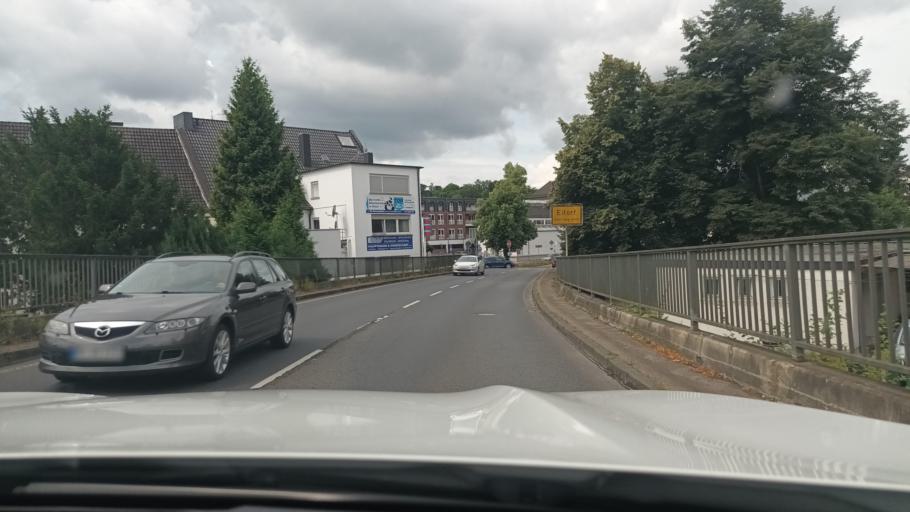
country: DE
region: North Rhine-Westphalia
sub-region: Regierungsbezirk Koln
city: Eitorf
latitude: 50.7714
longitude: 7.4525
